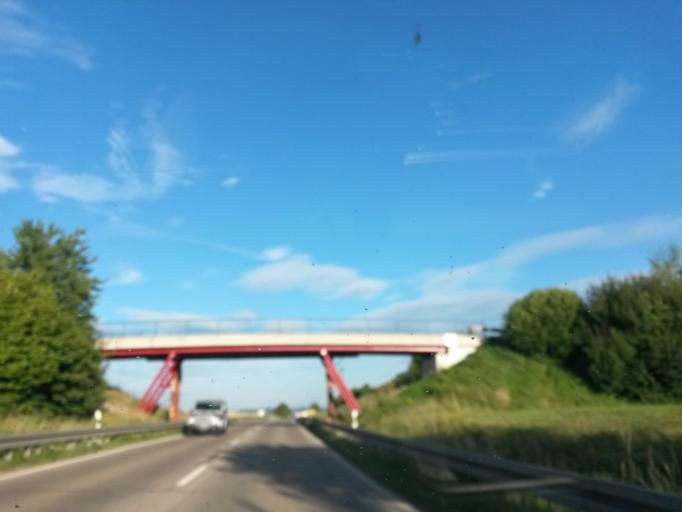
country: DE
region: Baden-Wuerttemberg
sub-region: Regierungsbezirk Stuttgart
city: Ellwangen
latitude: 48.9608
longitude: 10.1692
